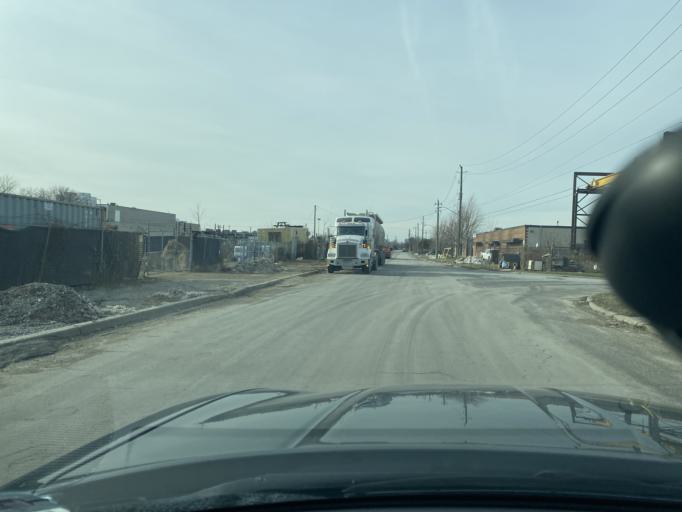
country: CA
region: Ontario
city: Scarborough
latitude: 43.7205
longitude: -79.2805
